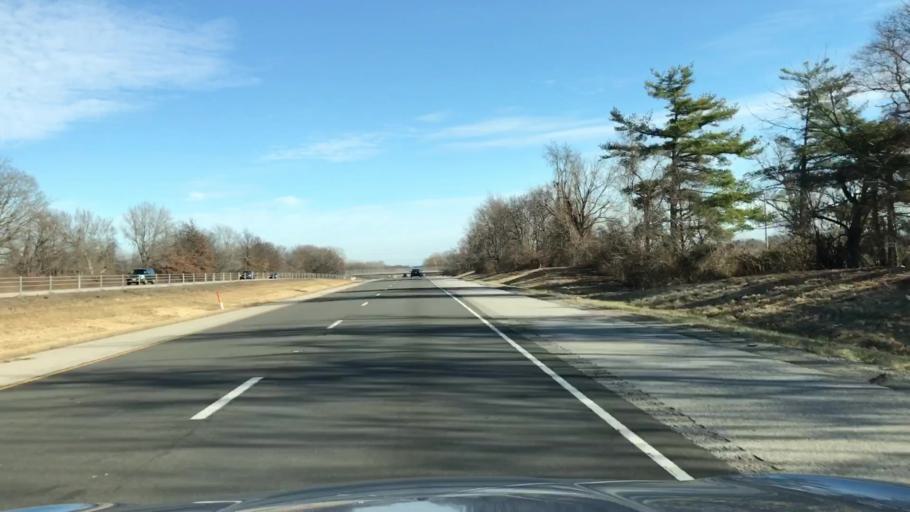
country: US
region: Illinois
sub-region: Madison County
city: Glen Carbon
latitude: 38.7565
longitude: -89.9903
